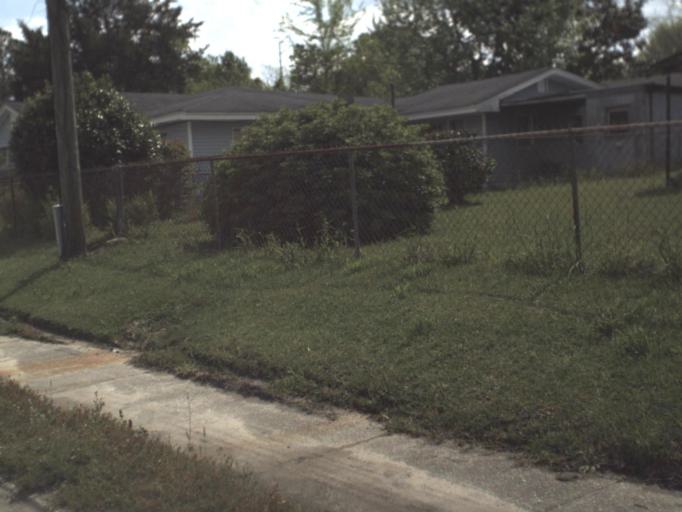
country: US
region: Alabama
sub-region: Escambia County
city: Flomaton
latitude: 30.9892
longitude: -87.2570
